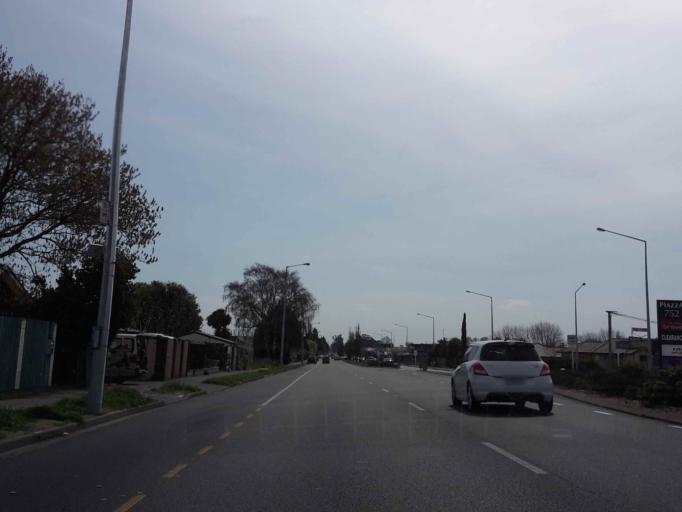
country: NZ
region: Canterbury
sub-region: Waimakariri District
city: Kaiapoi
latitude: -43.4497
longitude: 172.6292
